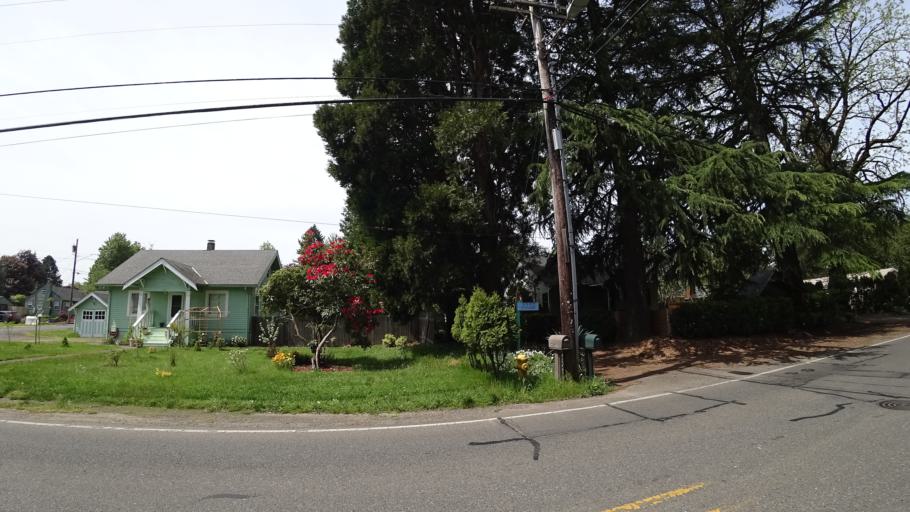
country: US
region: Oregon
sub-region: Clackamas County
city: Milwaukie
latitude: 45.4504
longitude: -122.6185
